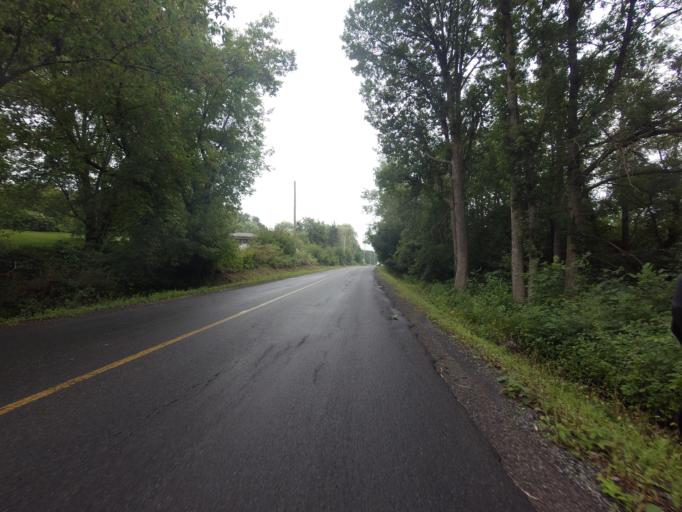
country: CA
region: Ontario
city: Bells Corners
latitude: 45.3417
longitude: -76.0089
